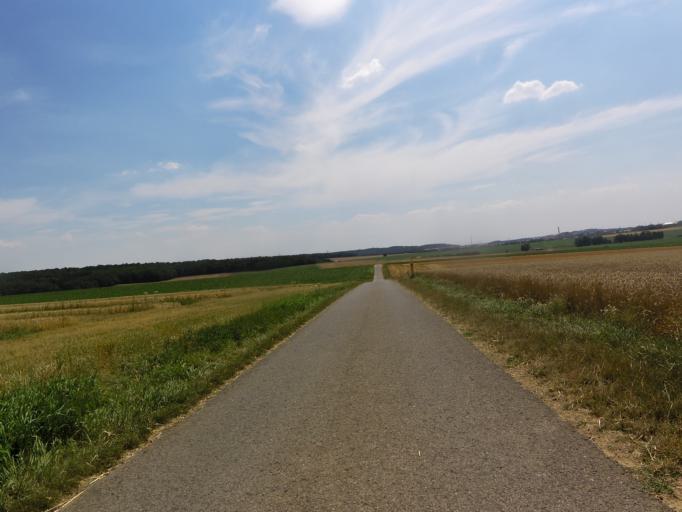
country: DE
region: Bavaria
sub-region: Regierungsbezirk Unterfranken
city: Estenfeld
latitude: 49.8170
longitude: 10.0110
